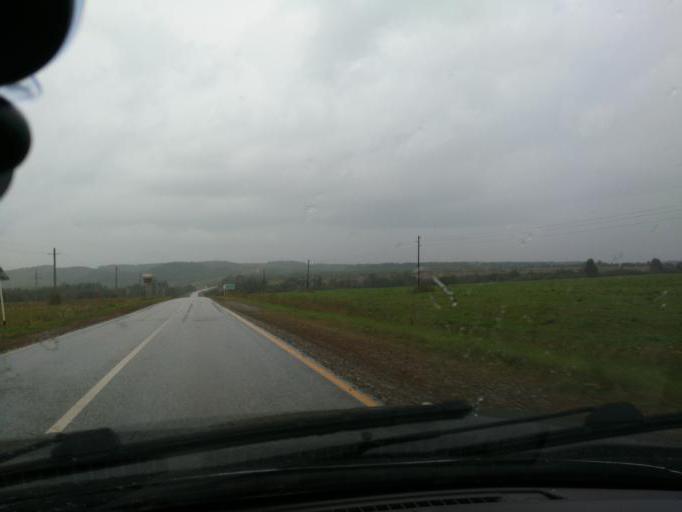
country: RU
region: Perm
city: Barda
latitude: 57.1027
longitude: 55.5278
